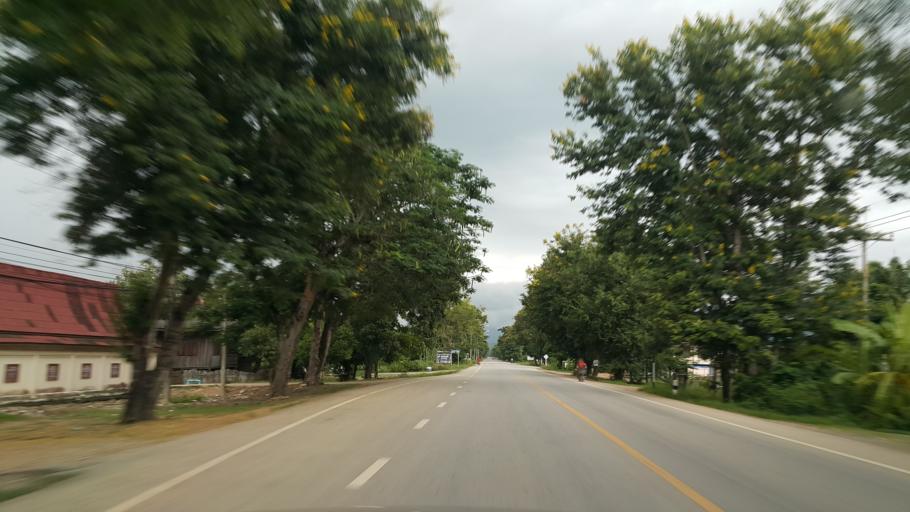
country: TH
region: Phayao
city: Dok Kham Tai
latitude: 19.2012
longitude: 100.0322
